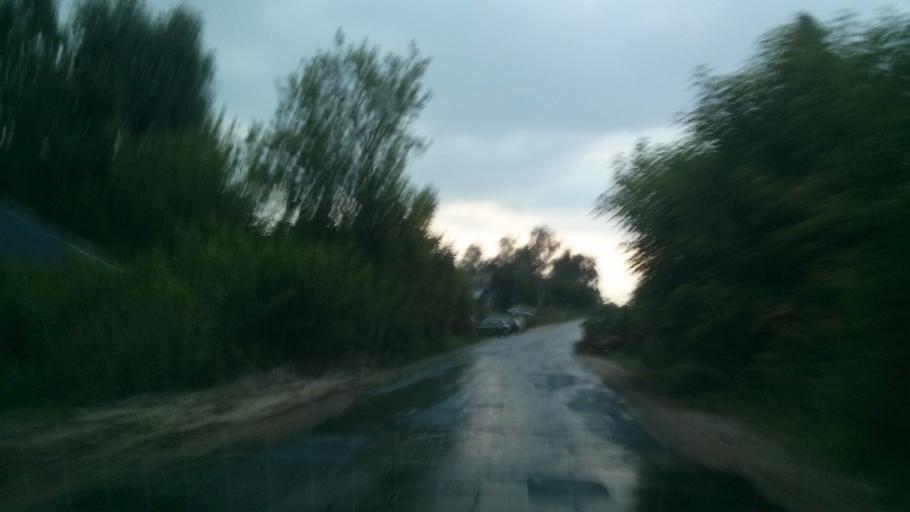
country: RU
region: Nizjnij Novgorod
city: Shimorskoye
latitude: 55.3570
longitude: 41.9325
